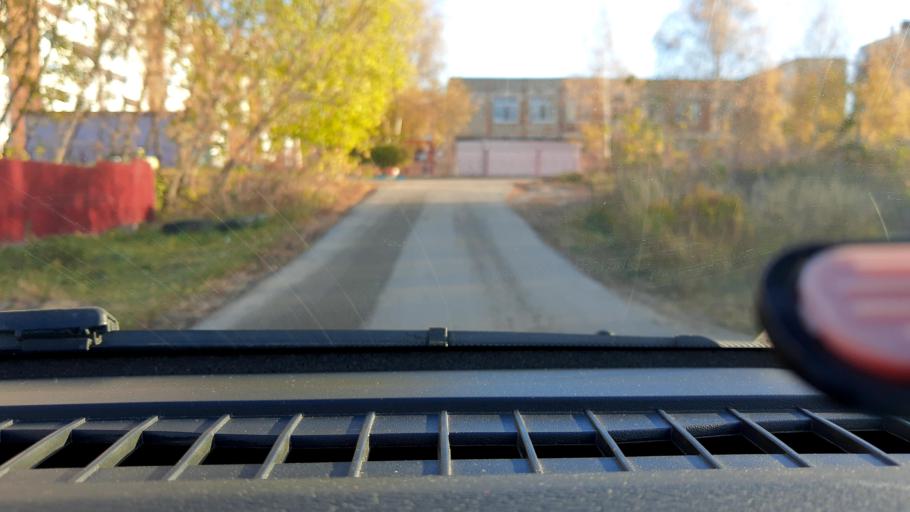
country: RU
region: Nizjnij Novgorod
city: Gorbatovka
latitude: 56.3698
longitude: 43.8059
